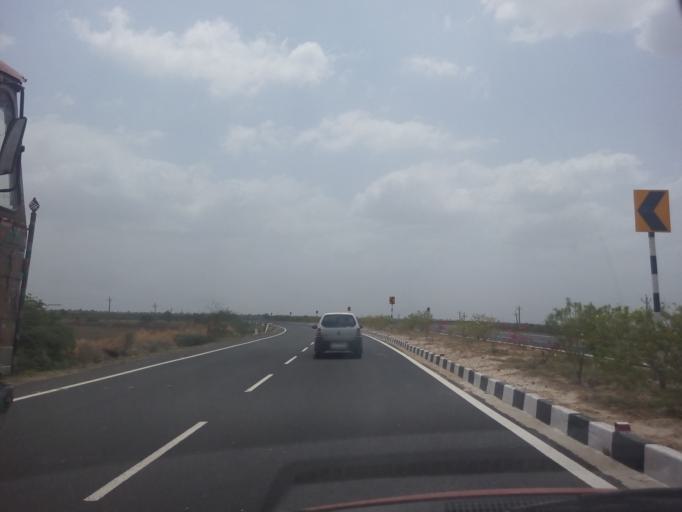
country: IN
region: Gujarat
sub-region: Ahmadabad
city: Mandal
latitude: 23.0801
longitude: 71.8337
